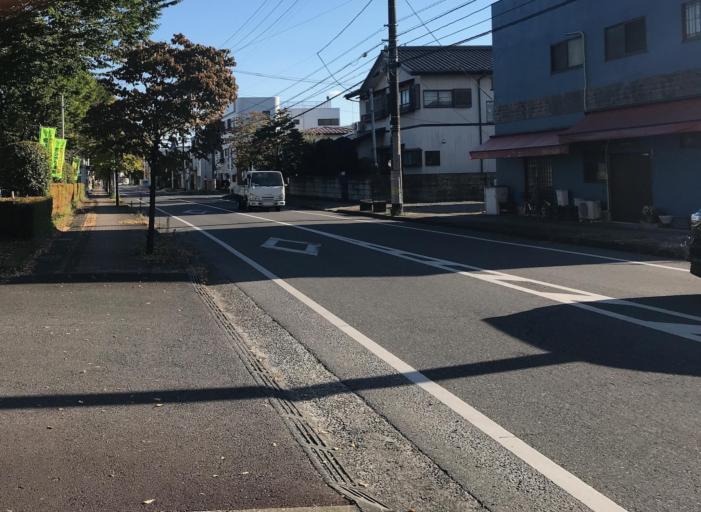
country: JP
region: Tochigi
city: Kanuma
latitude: 36.5694
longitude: 139.7514
